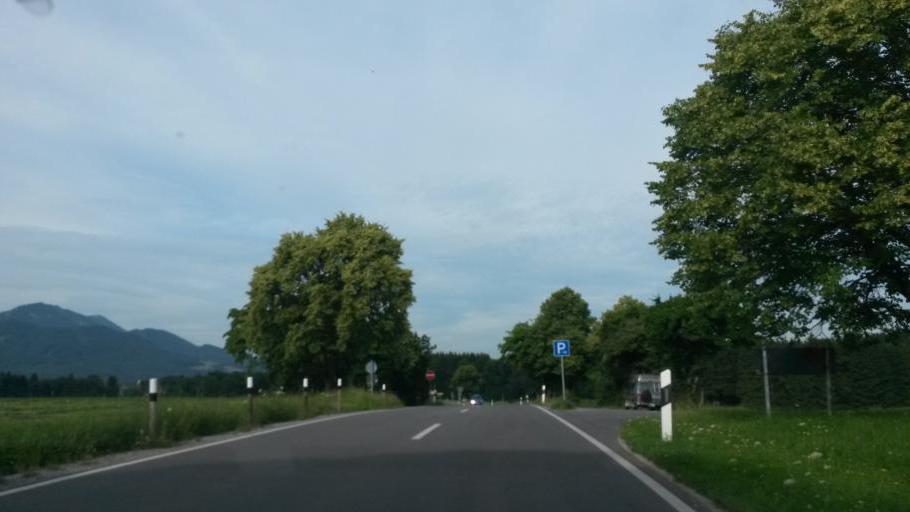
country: DE
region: Bavaria
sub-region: Upper Bavaria
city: Prien am Chiemsee
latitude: 47.8226
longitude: 12.3413
